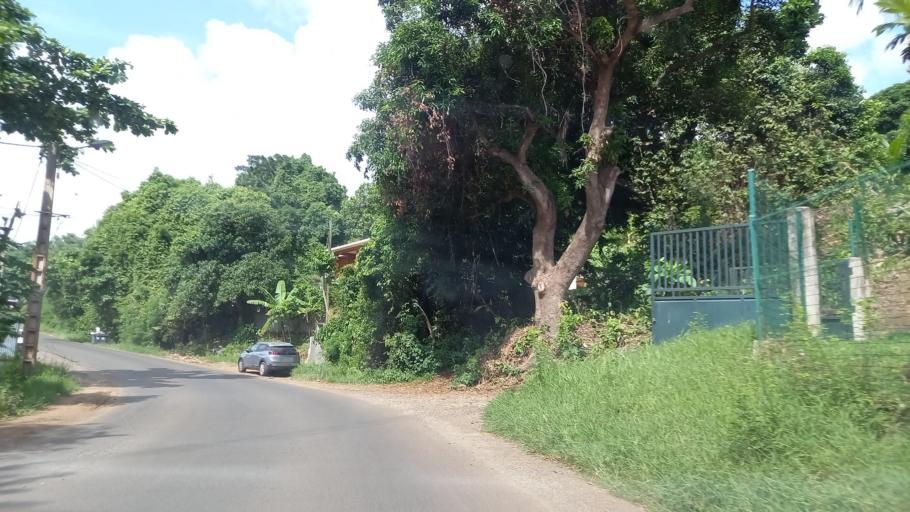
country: YT
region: Sada
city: Sada
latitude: -12.8556
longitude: 45.1031
